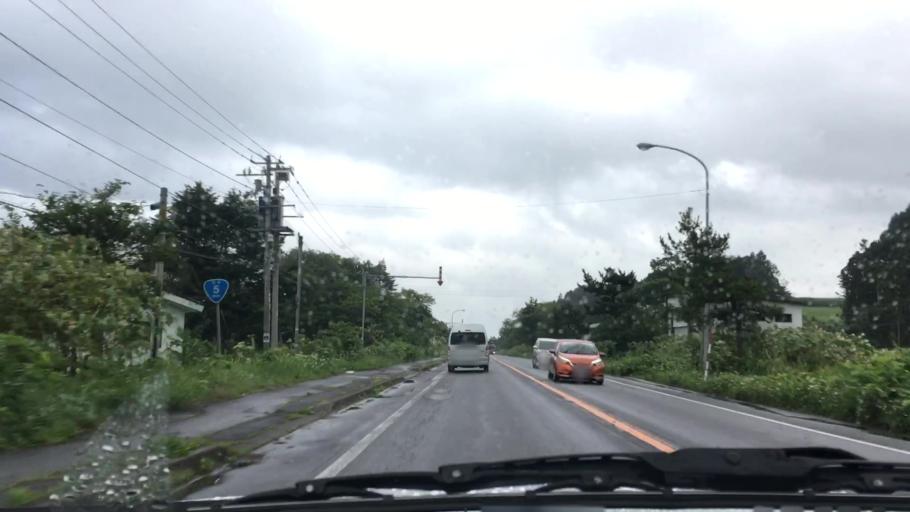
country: JP
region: Hokkaido
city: Nanae
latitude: 42.2239
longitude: 140.3521
